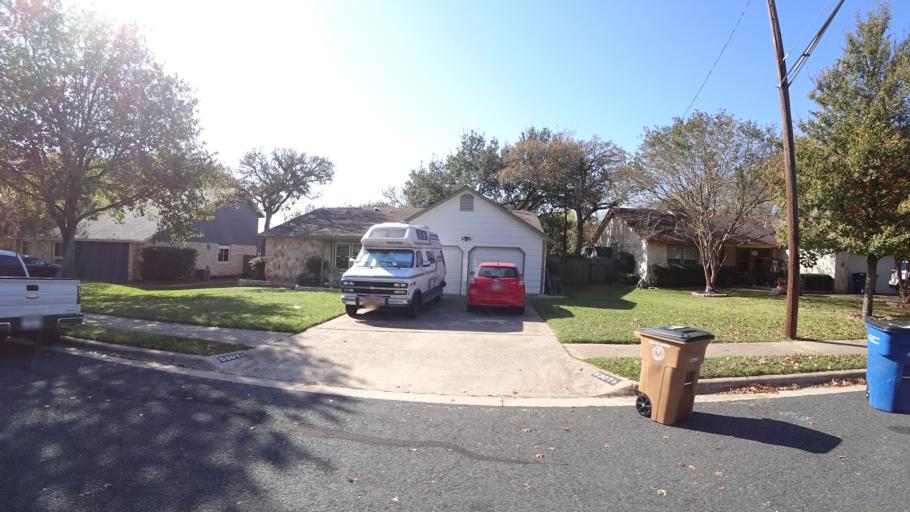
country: US
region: Texas
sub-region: Travis County
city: Barton Creek
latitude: 30.2296
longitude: -97.8506
